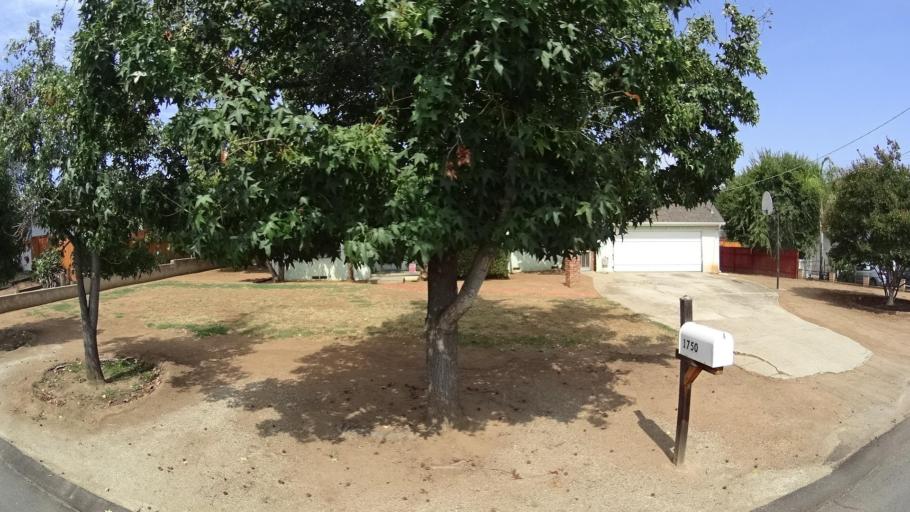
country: US
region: California
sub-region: San Diego County
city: Escondido
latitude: 33.1188
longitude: -117.0436
